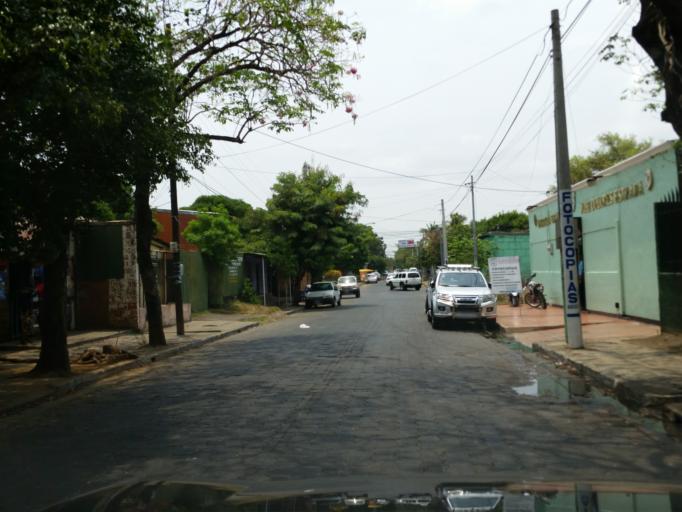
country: NI
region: Managua
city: Managua
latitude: 12.1506
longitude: -86.2461
